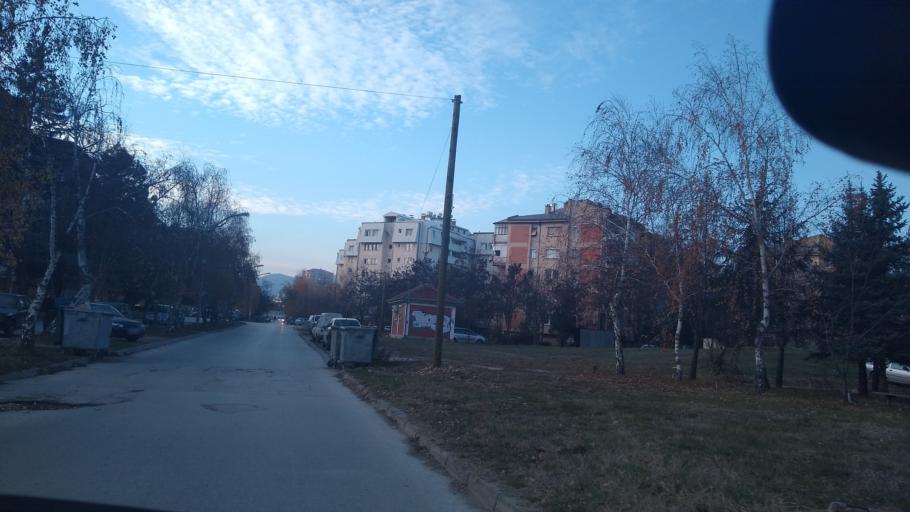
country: MK
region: Bitola
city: Bitola
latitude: 41.0282
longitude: 21.3459
